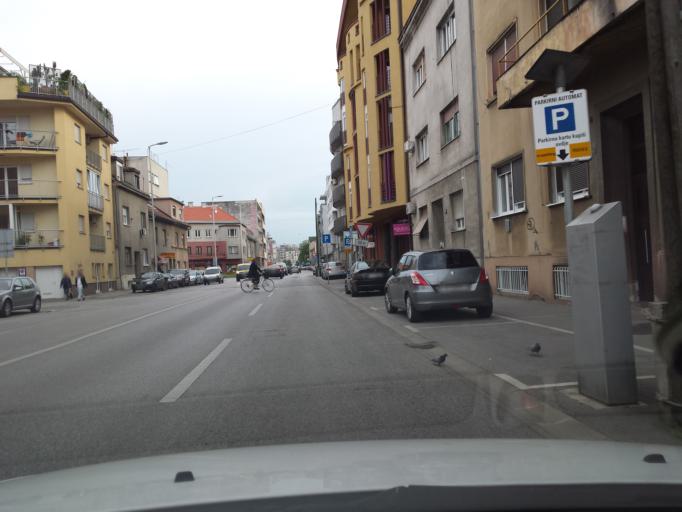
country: HR
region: Grad Zagreb
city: Zagreb - Centar
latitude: 45.8049
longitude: 15.9546
